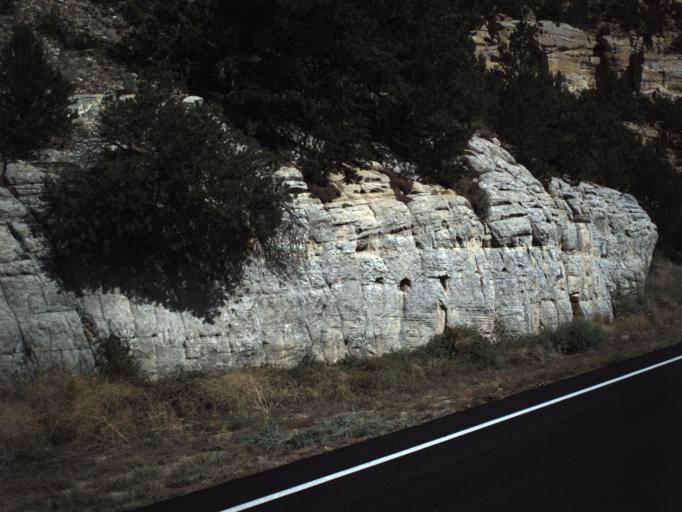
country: US
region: Utah
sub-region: Wayne County
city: Loa
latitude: 37.7415
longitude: -111.7244
